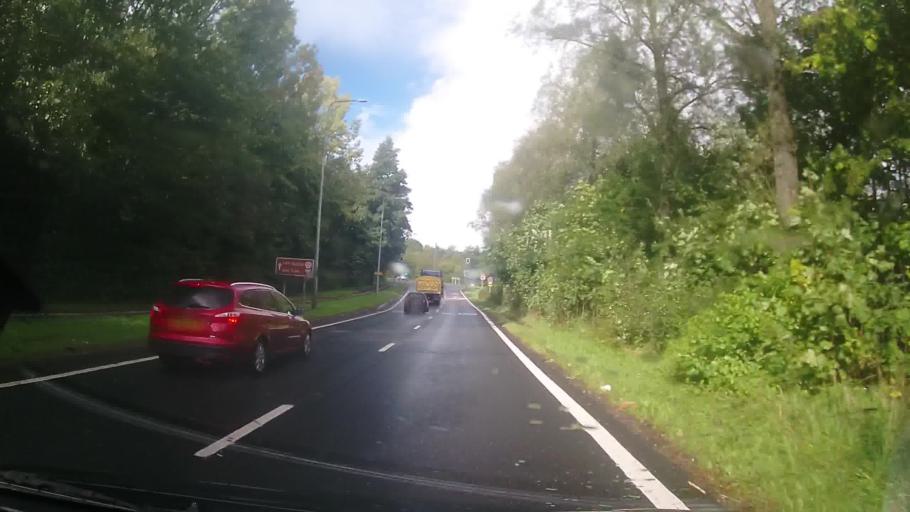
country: GB
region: England
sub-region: Shropshire
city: Hadley
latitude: 52.6940
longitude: -2.4914
